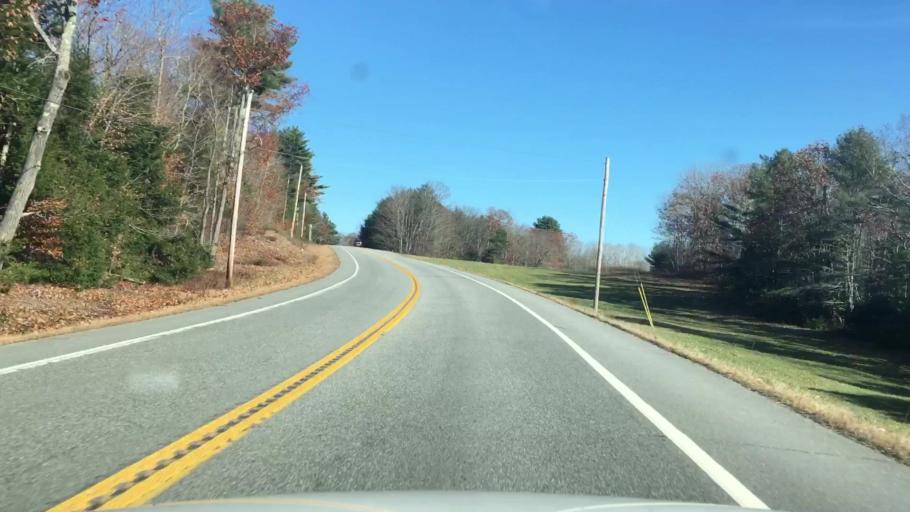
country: US
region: Maine
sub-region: Lincoln County
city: Jefferson
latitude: 44.2575
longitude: -69.4716
